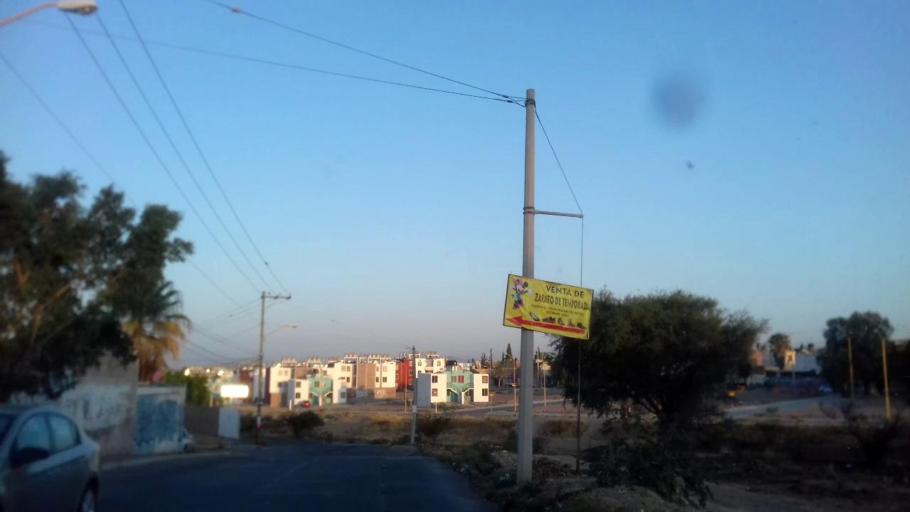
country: MX
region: Aguascalientes
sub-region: Aguascalientes
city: San Sebastian [Fraccionamiento]
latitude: 21.8503
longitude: -102.2579
